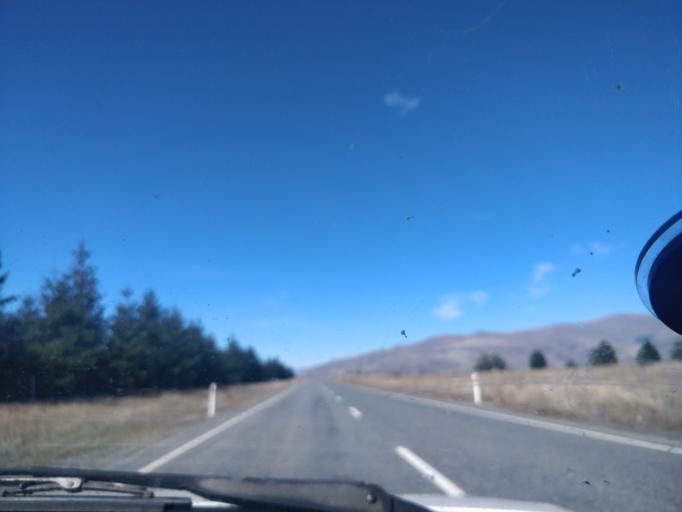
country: NZ
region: Otago
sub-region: Queenstown-Lakes District
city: Wanaka
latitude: -44.2681
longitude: 170.0399
